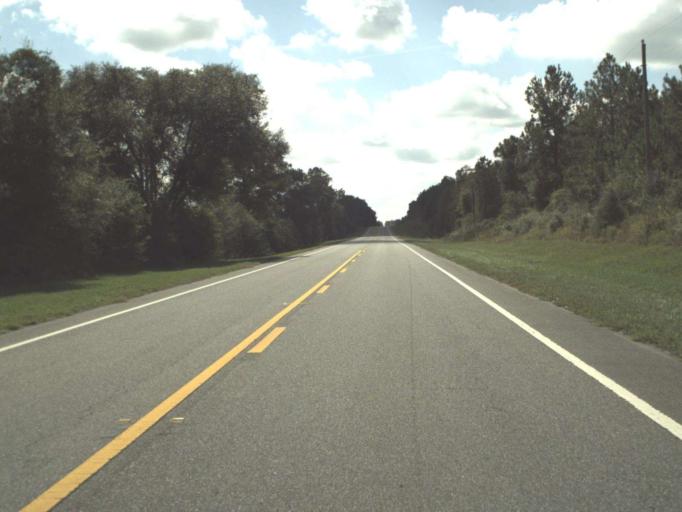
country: US
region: Florida
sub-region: Walton County
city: DeFuniak Springs
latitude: 30.8178
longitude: -85.9582
